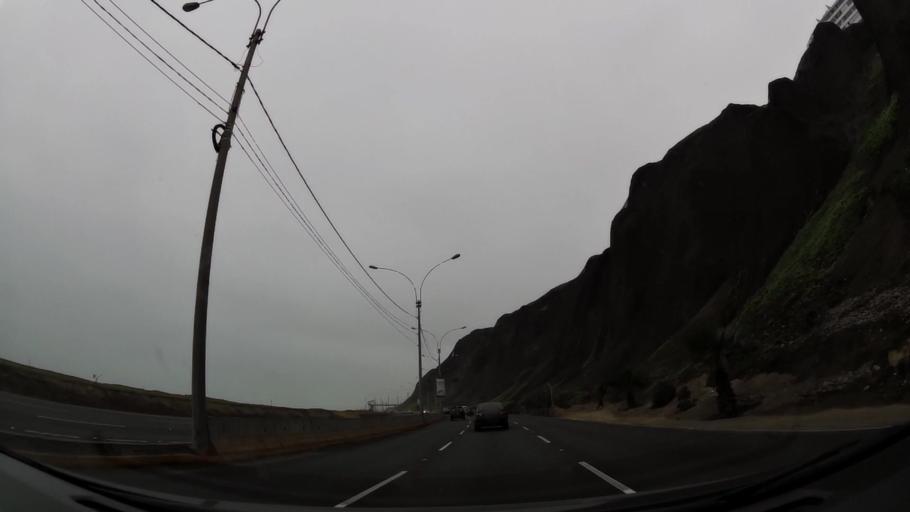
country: PE
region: Lima
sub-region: Lima
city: San Isidro
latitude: -12.1193
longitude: -77.0459
